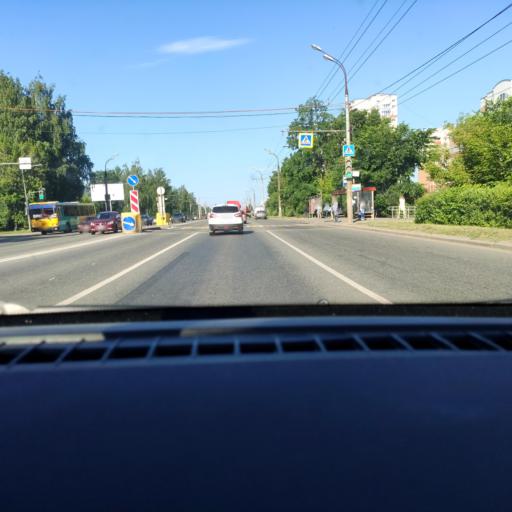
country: RU
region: Udmurtiya
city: Izhevsk
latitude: 56.8889
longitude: 53.2470
